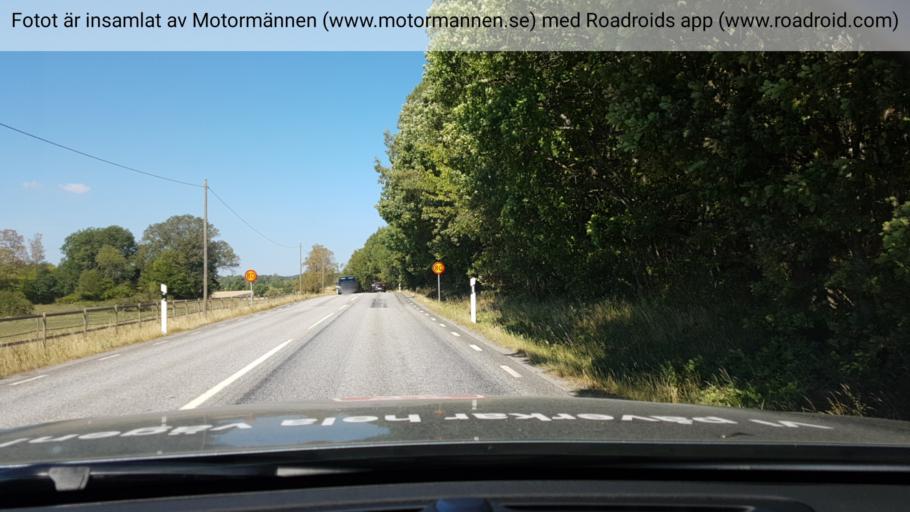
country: SE
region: Stockholm
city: Stenhamra
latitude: 59.2898
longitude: 17.7021
